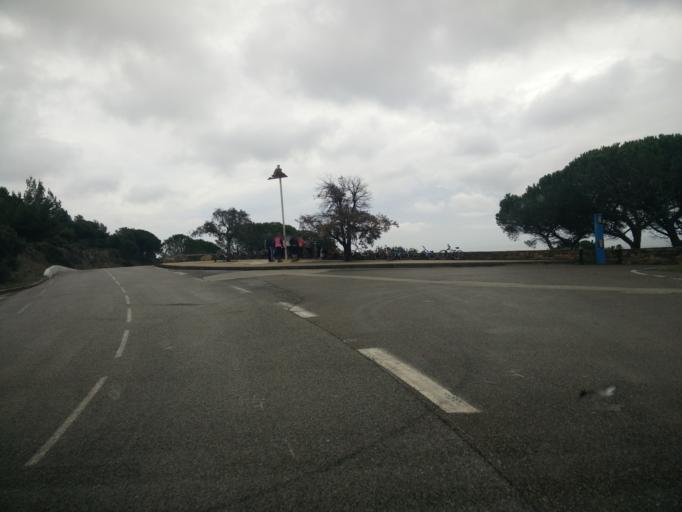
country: FR
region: Provence-Alpes-Cote d'Azur
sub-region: Departement du Var
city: Six-Fours-les-Plages
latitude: 43.0588
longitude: 5.8575
